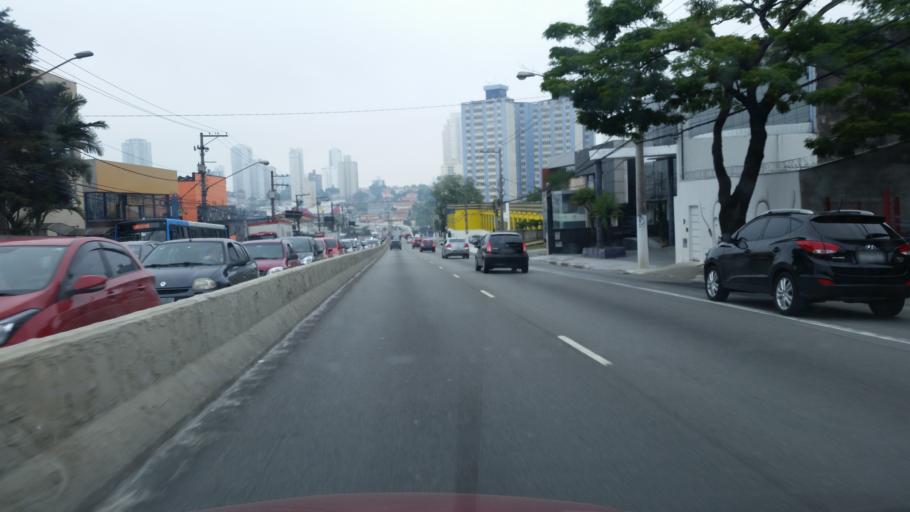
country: BR
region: Sao Paulo
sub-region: Diadema
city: Diadema
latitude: -23.6483
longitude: -46.6759
